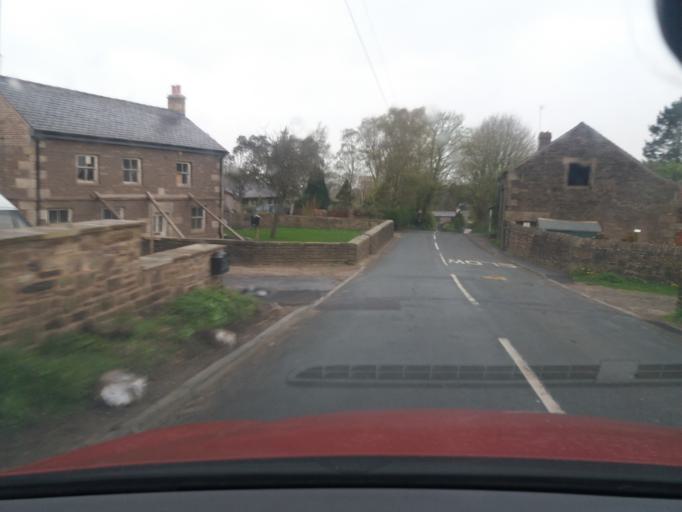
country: GB
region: England
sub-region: Lancashire
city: Chorley
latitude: 53.6838
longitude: -2.6205
